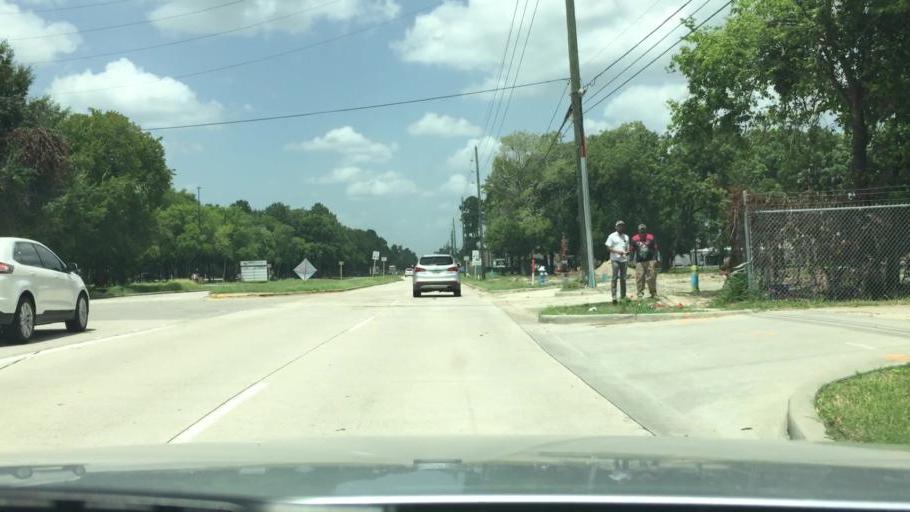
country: US
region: Texas
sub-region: Harris County
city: Hudson
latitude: 29.9640
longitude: -95.5303
